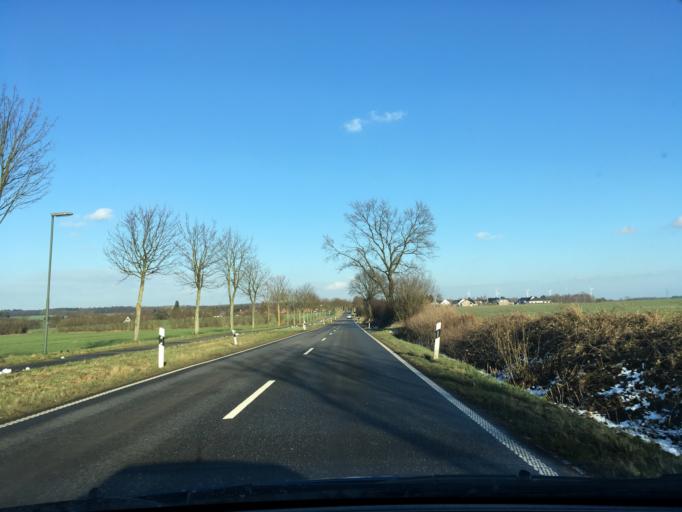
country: DE
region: Schleswig-Holstein
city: Krukow
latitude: 53.4367
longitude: 10.4749
